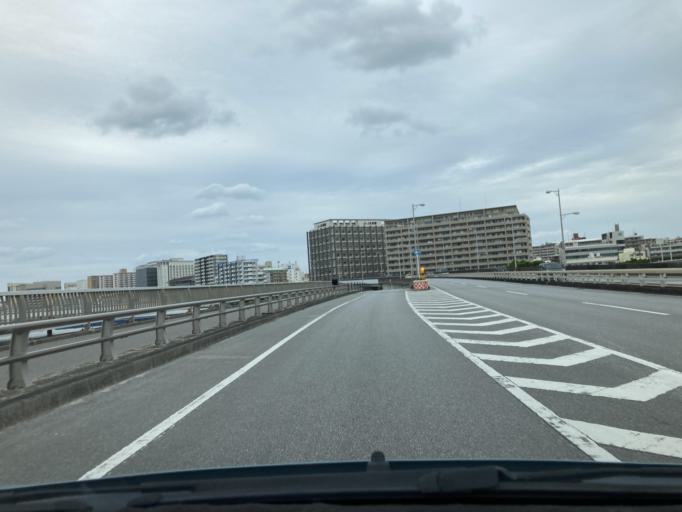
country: JP
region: Okinawa
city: Naha-shi
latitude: 26.1996
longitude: 127.6796
